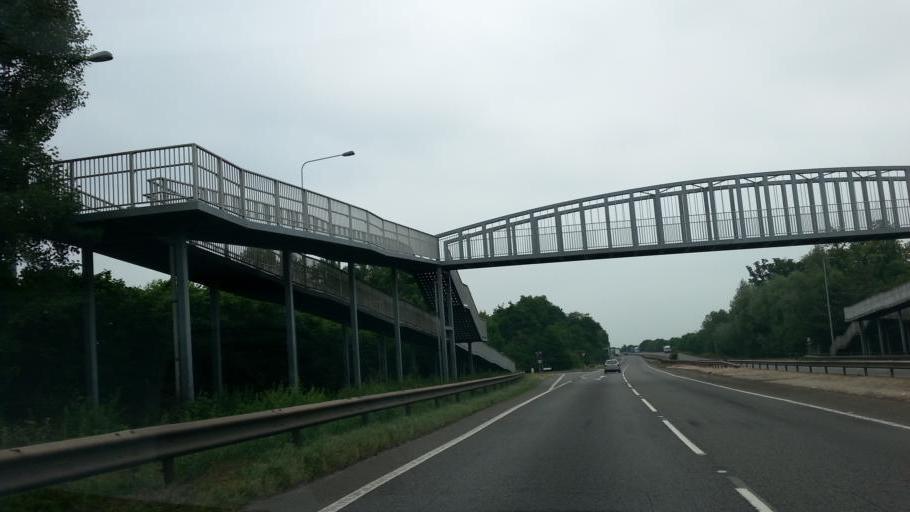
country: GB
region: England
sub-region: Derbyshire
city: Rodsley
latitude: 52.8840
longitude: -1.7256
